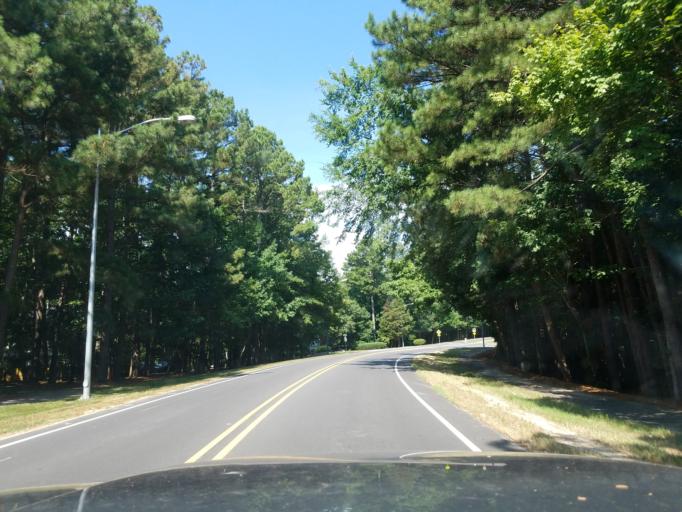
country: US
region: North Carolina
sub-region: Durham County
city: Durham
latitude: 35.9213
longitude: -78.9334
